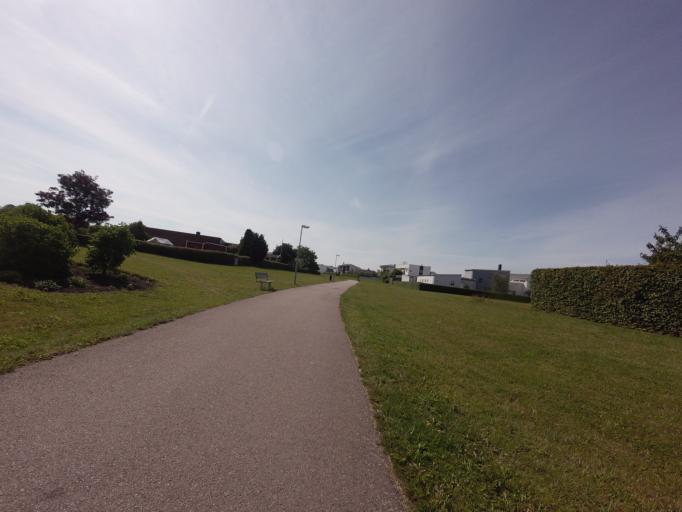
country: SE
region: Skane
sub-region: Helsingborg
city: Glumslov
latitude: 55.9474
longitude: 12.8023
